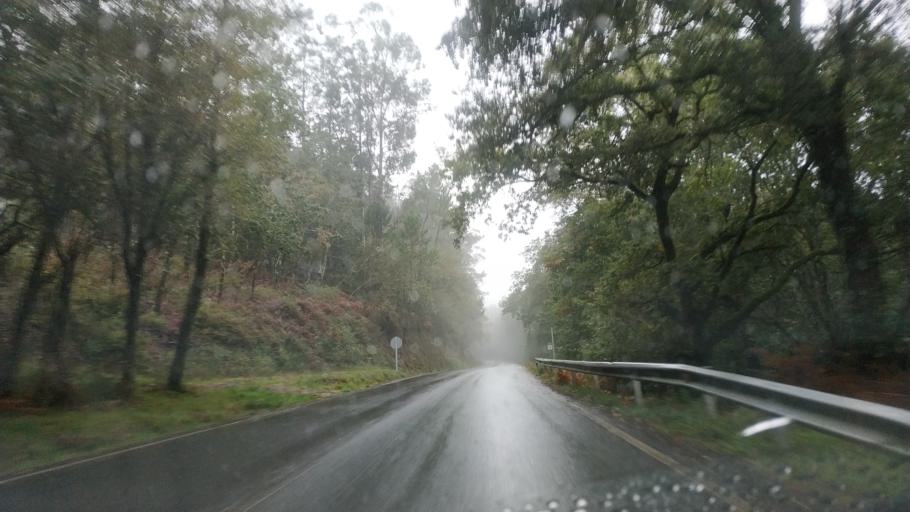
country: ES
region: Galicia
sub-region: Provincia da Coruna
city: Negreira
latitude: 42.9098
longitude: -8.7500
